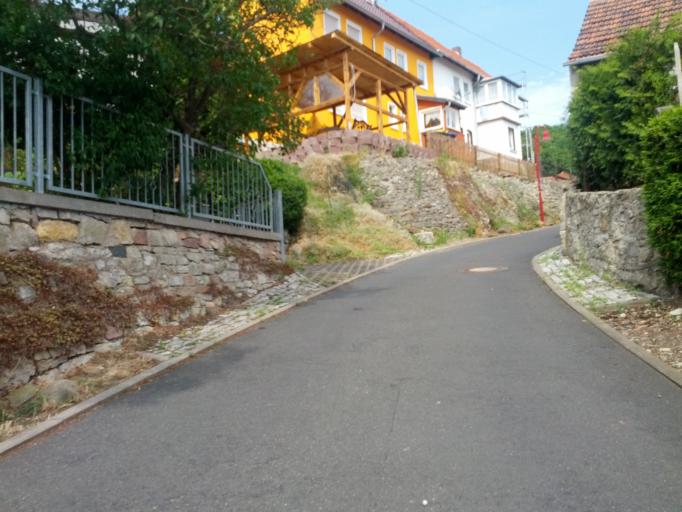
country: DE
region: Thuringia
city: Krauthausen
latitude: 50.9928
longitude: 10.2594
